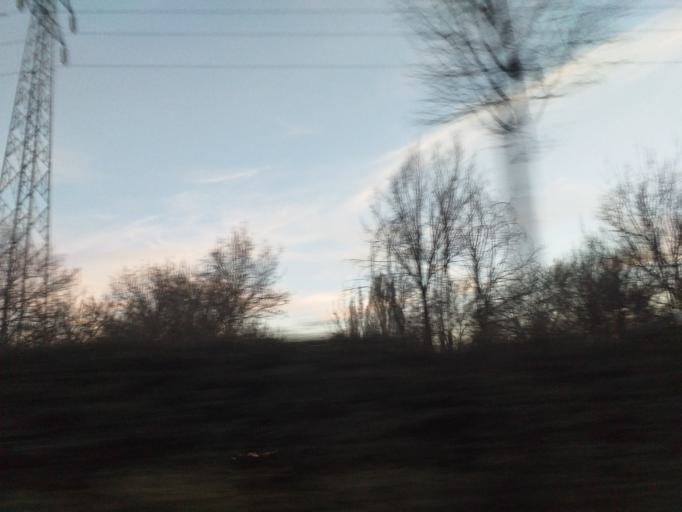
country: TR
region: Ankara
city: Ankara
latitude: 39.9544
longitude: 32.8182
